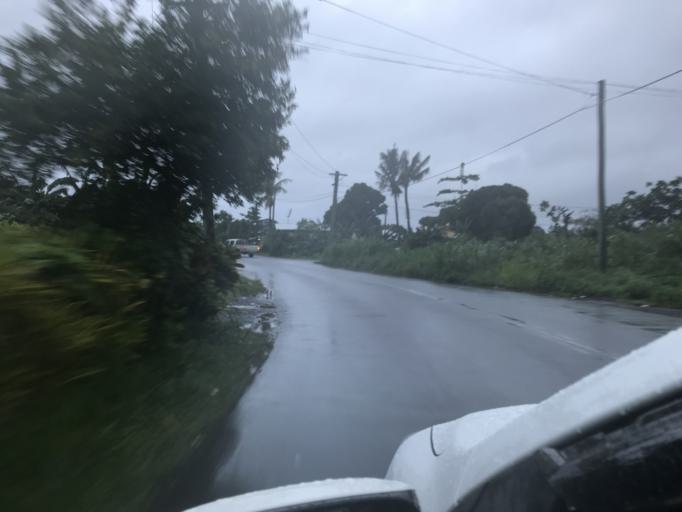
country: WS
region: Tuamasaga
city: Apia
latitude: -13.8372
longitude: -171.7577
